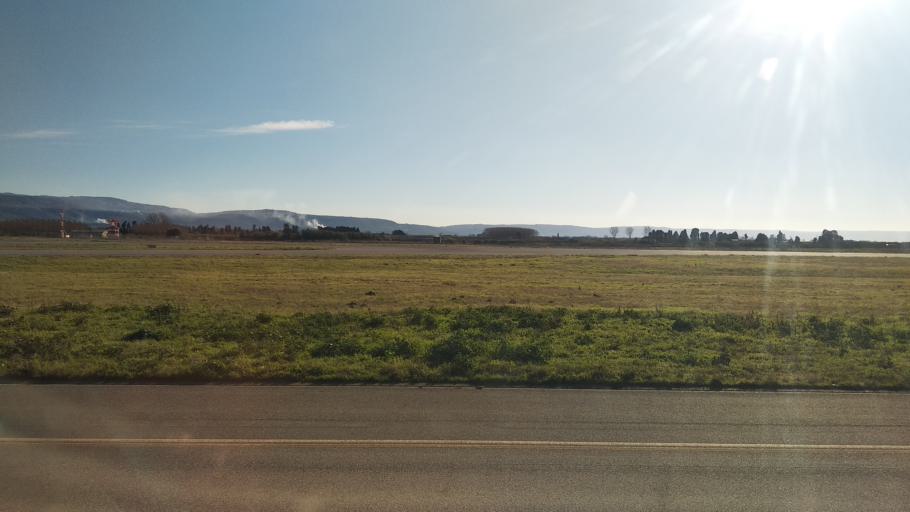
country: IT
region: Calabria
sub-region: Provincia di Catanzaro
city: Santa Eufemia Lamezia
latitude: 38.9068
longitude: 16.2492
